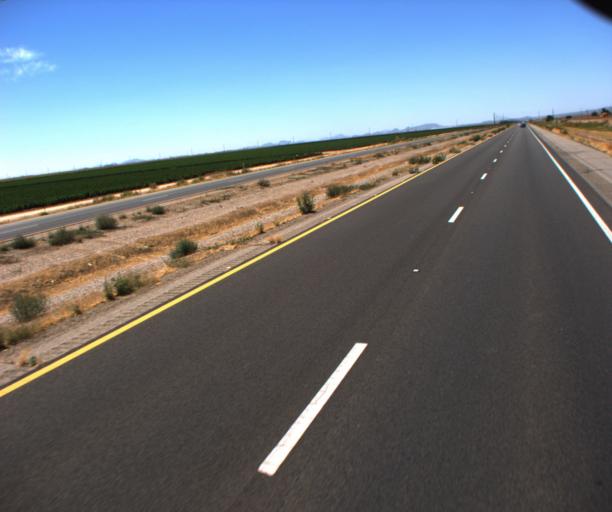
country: US
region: Arizona
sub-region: Pinal County
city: Maricopa
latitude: 32.9944
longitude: -112.0481
